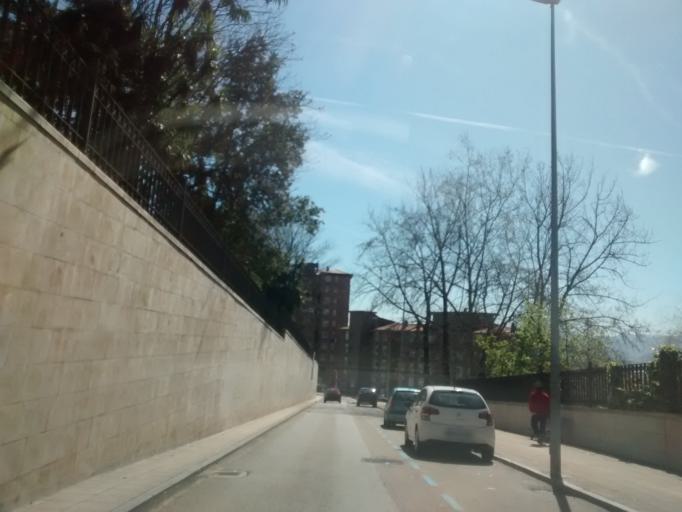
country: ES
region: Cantabria
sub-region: Provincia de Cantabria
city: Santander
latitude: 43.4671
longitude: -3.8130
